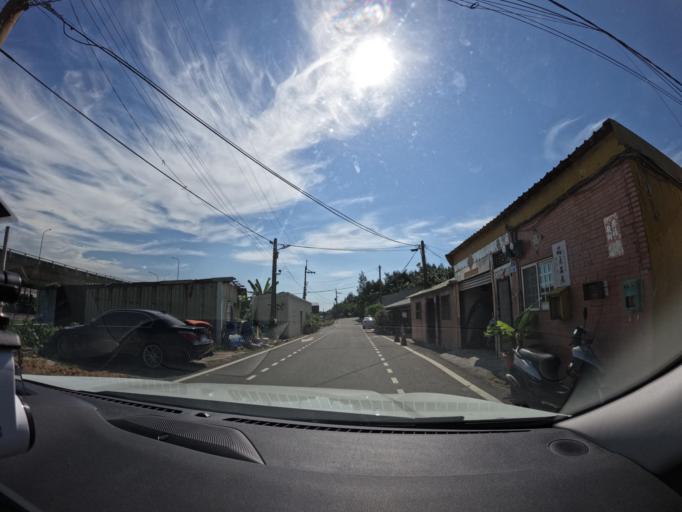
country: TW
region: Taiwan
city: Taoyuan City
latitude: 25.1120
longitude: 121.2384
